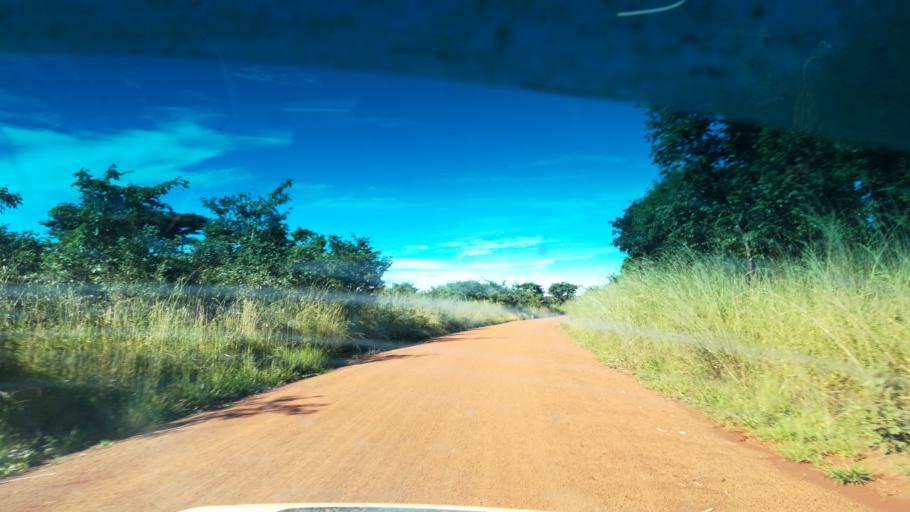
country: ZM
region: Luapula
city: Nchelenge
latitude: -9.3127
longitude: 28.2526
